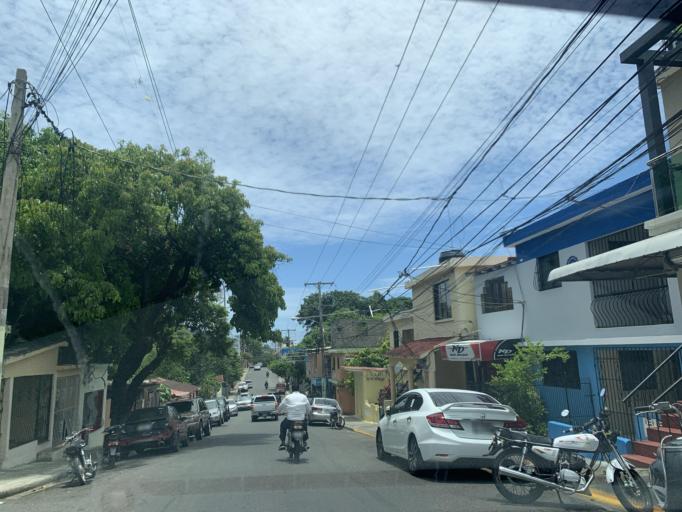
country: DO
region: Puerto Plata
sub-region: Puerto Plata
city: Puerto Plata
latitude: 19.7909
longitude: -70.6848
